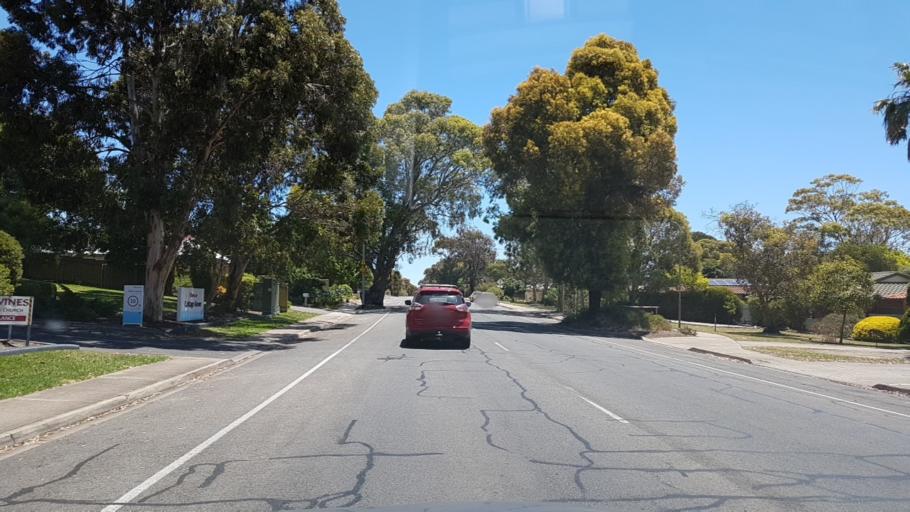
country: AU
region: South Australia
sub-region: Marion
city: Trott Park
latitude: -35.0930
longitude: 138.5587
